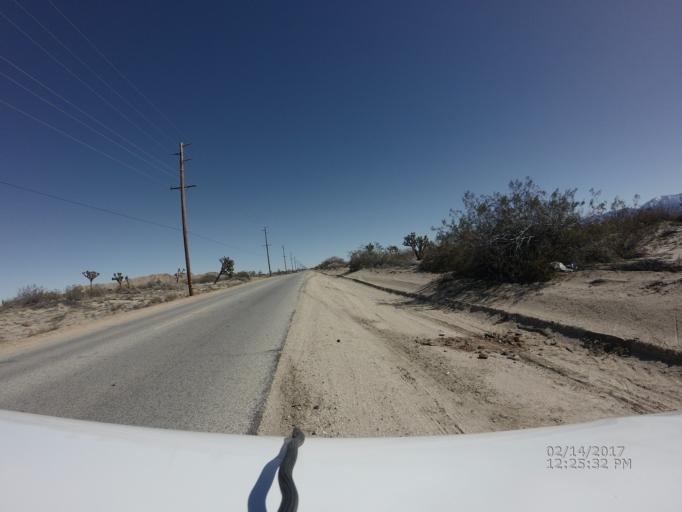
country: US
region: California
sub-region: Los Angeles County
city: Lake Los Angeles
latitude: 34.5800
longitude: -117.8955
